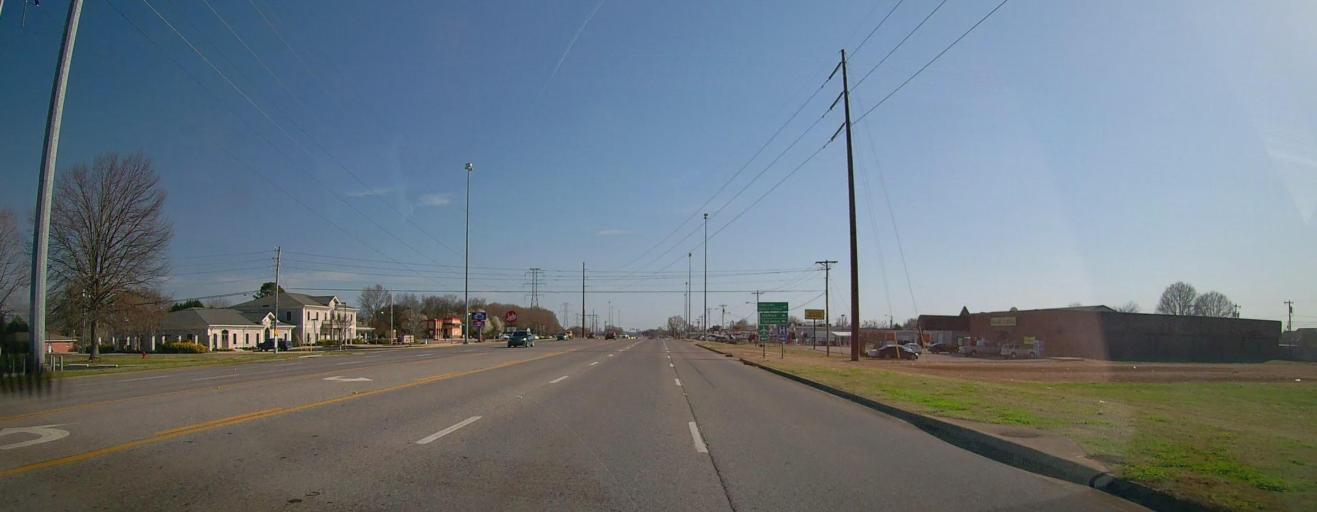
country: US
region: Alabama
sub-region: Colbert County
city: Muscle Shoals
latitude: 34.7486
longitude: -87.6353
